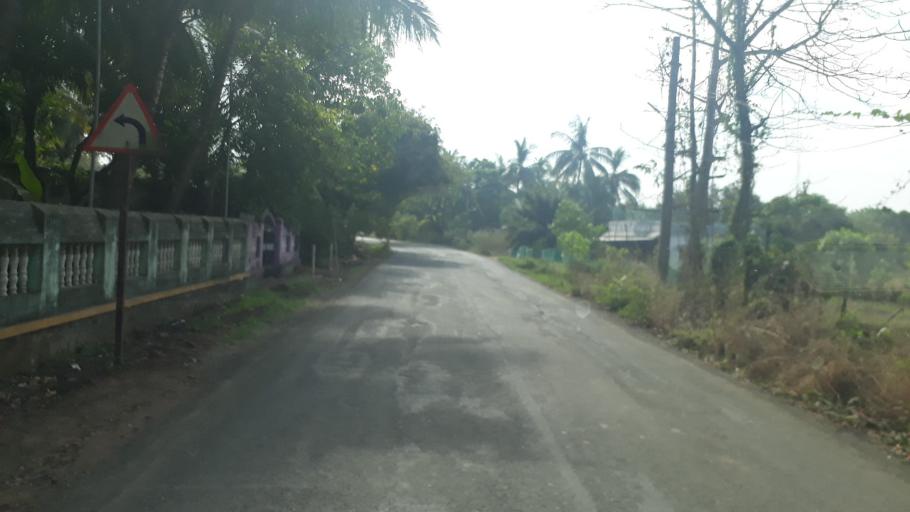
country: IN
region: Maharashtra
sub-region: Raigarh
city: Revadanda
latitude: 18.6006
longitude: 72.9187
